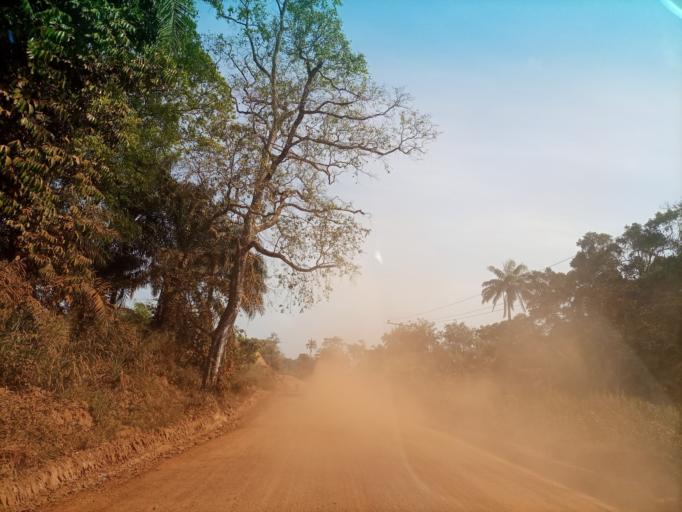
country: NG
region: Enugu
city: Eha Amufu
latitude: 6.6674
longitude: 7.7527
